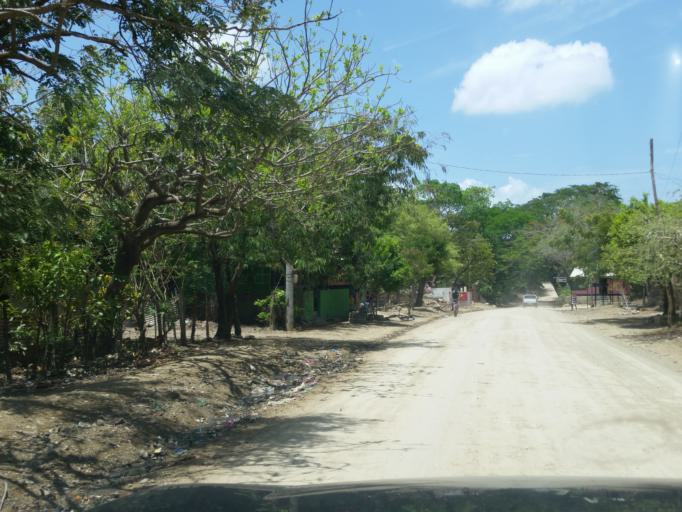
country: NI
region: Rivas
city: Tola
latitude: 11.4587
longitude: -86.0778
